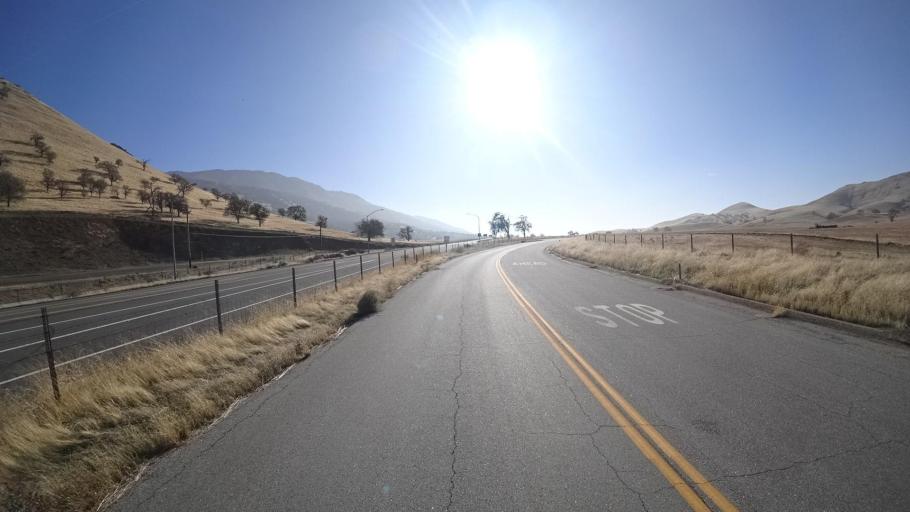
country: US
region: California
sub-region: Kern County
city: Bear Valley Springs
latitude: 35.2630
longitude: -118.6591
